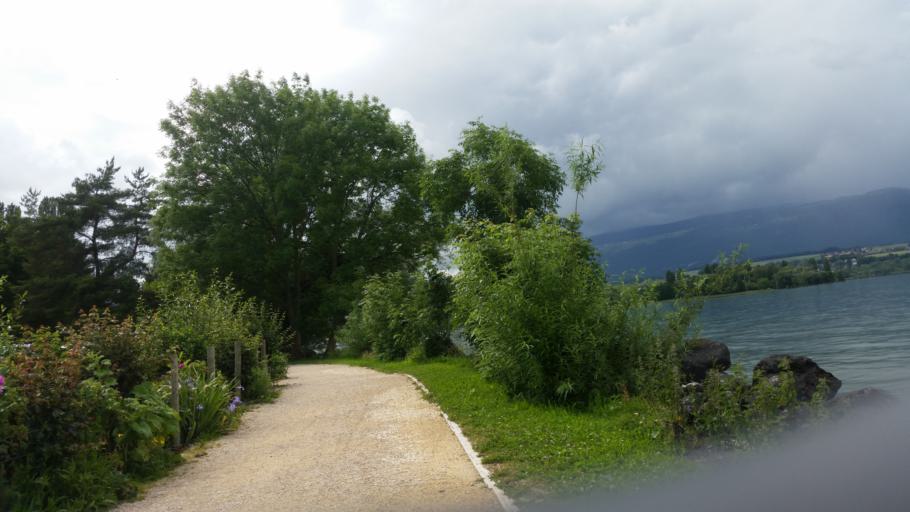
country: CH
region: Vaud
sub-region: Jura-Nord vaudois District
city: Yverdon-les-Bains
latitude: 46.7860
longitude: 6.6510
